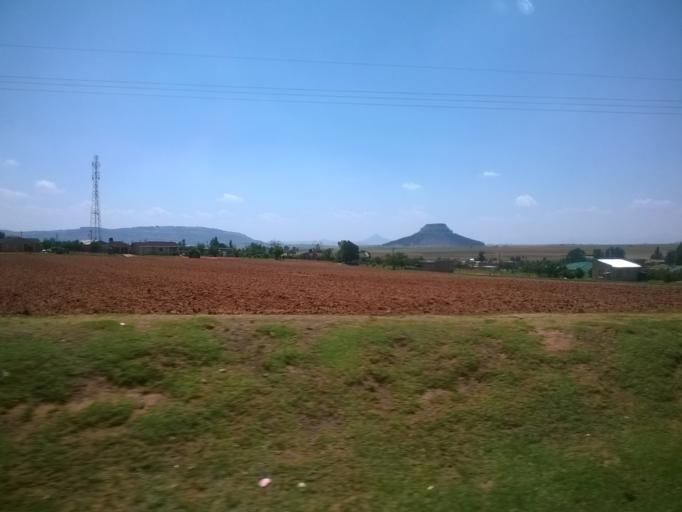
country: LS
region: Leribe
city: Maputsoe
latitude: -28.9710
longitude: 27.9701
